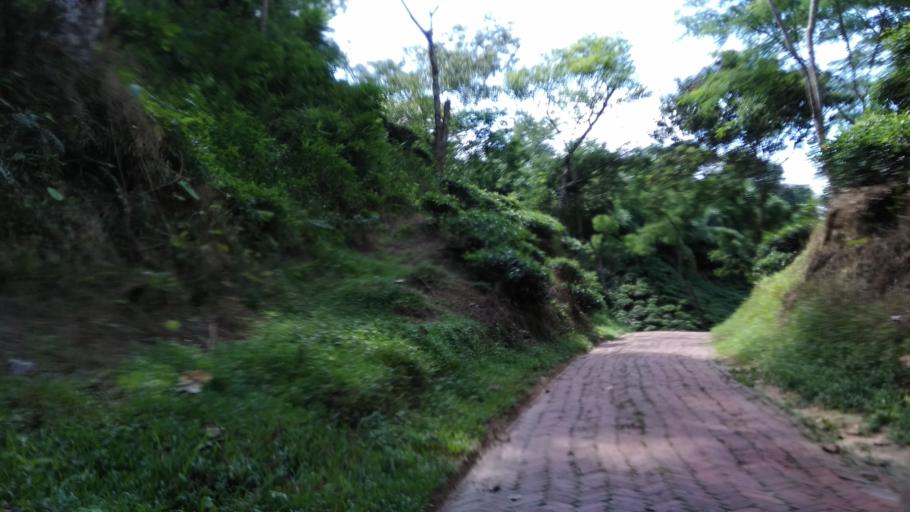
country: IN
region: Tripura
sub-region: Dhalai
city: Kamalpur
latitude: 24.3047
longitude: 91.8036
